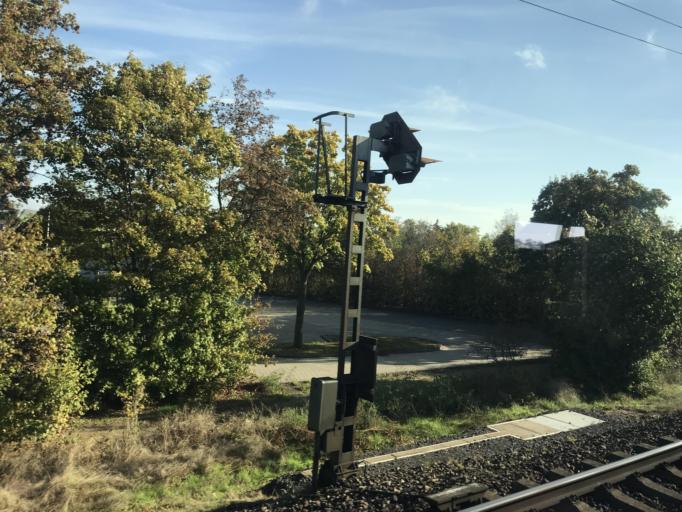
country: DE
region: Hesse
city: Weiterstadt
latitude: 49.9115
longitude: 8.5685
